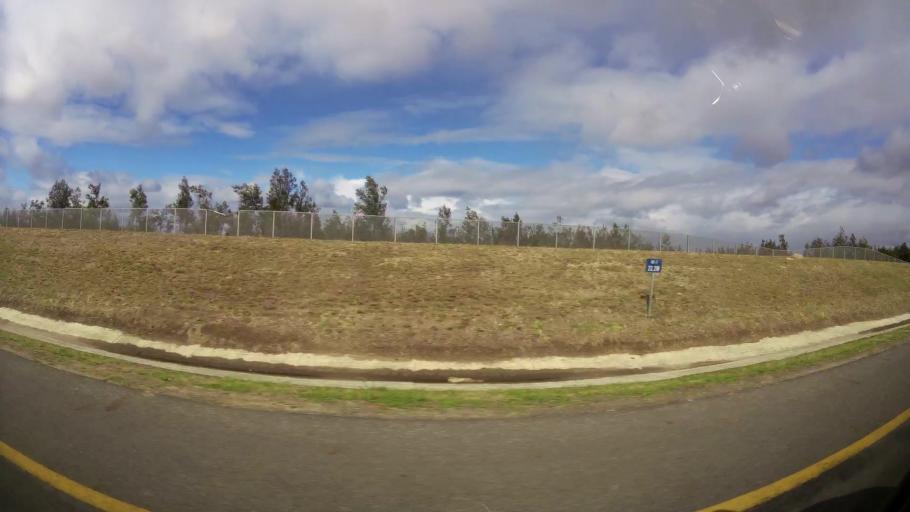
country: ZA
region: Western Cape
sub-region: Eden District Municipality
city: George
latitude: -33.9978
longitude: 22.4494
